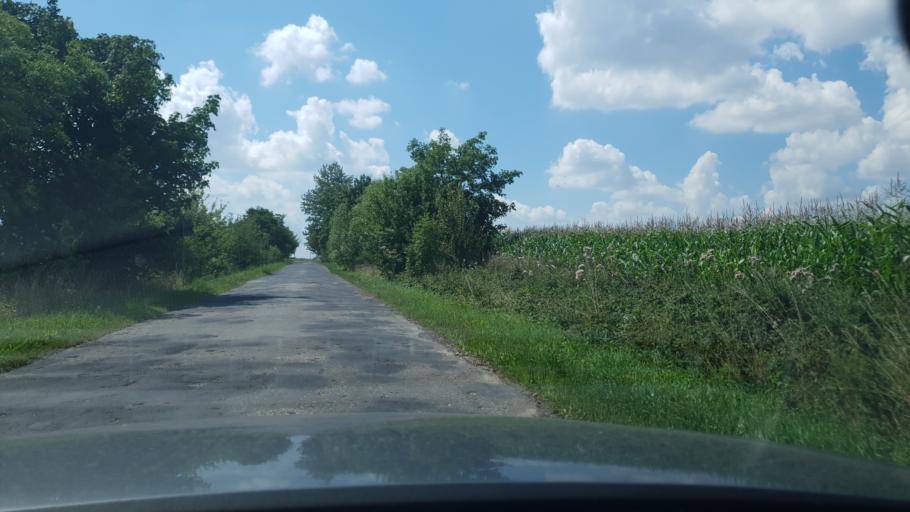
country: PL
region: Kujawsko-Pomorskie
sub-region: Powiat wabrzeski
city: Pluznica
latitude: 53.3183
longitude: 18.8250
